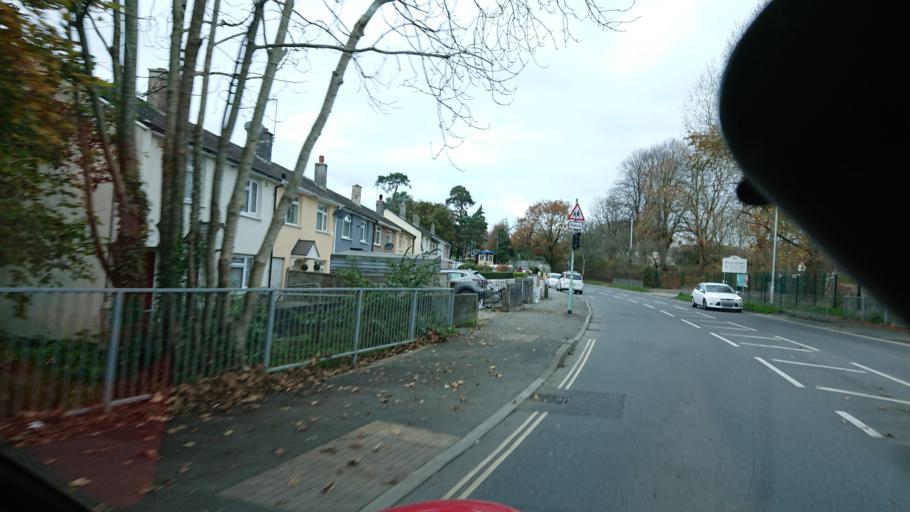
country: GB
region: England
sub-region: Plymouth
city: Plymouth
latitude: 50.4092
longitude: -4.1562
